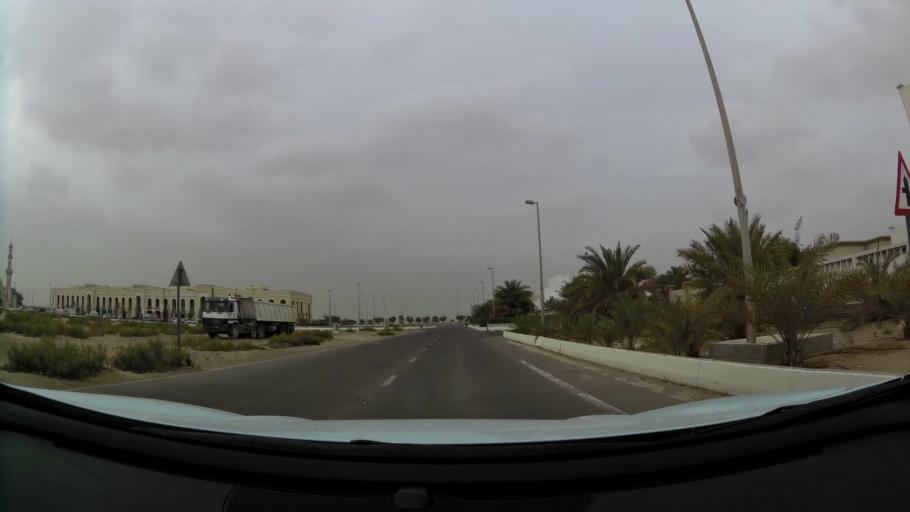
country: AE
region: Abu Dhabi
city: Abu Dhabi
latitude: 24.3758
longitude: 54.6621
